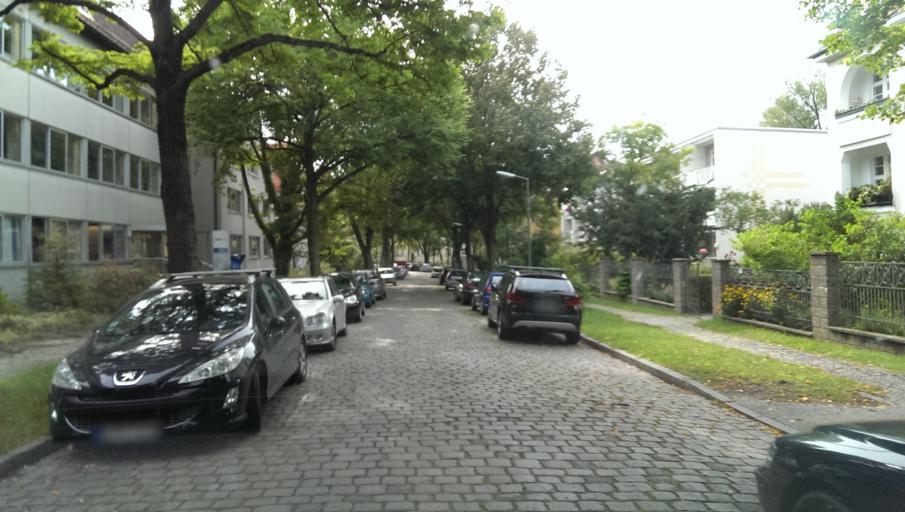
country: DE
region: Berlin
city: Zehlendorf Bezirk
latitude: 52.4312
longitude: 13.2512
